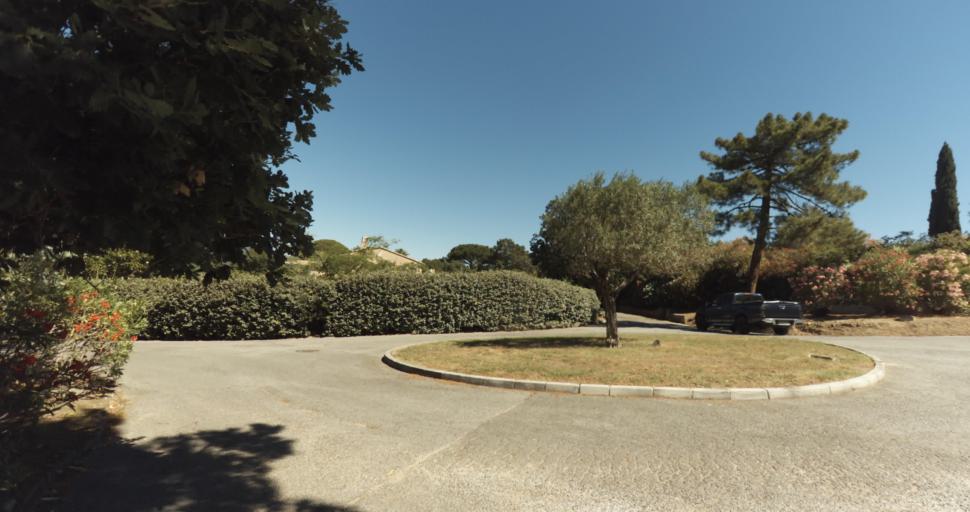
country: FR
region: Provence-Alpes-Cote d'Azur
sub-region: Departement du Var
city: Gassin
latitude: 43.2574
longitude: 6.5995
